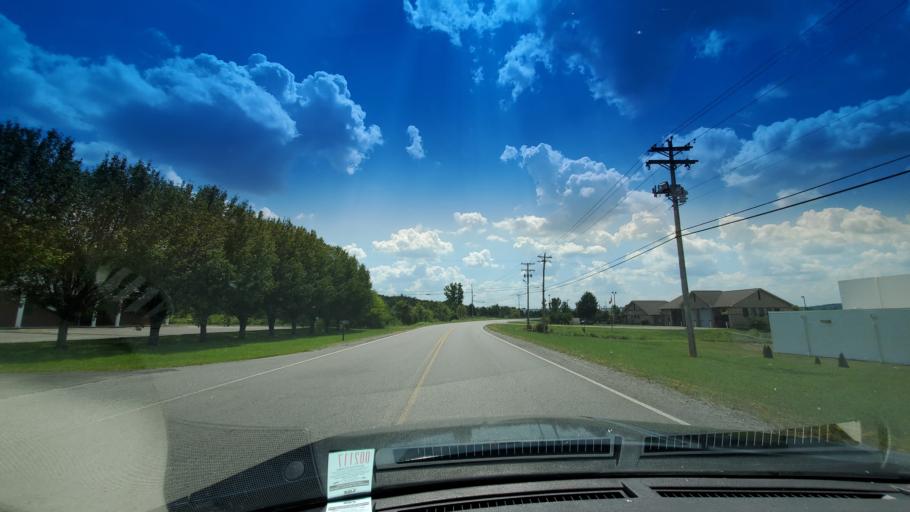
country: US
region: Tennessee
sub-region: Wilson County
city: Lebanon
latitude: 36.1750
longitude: -86.2858
